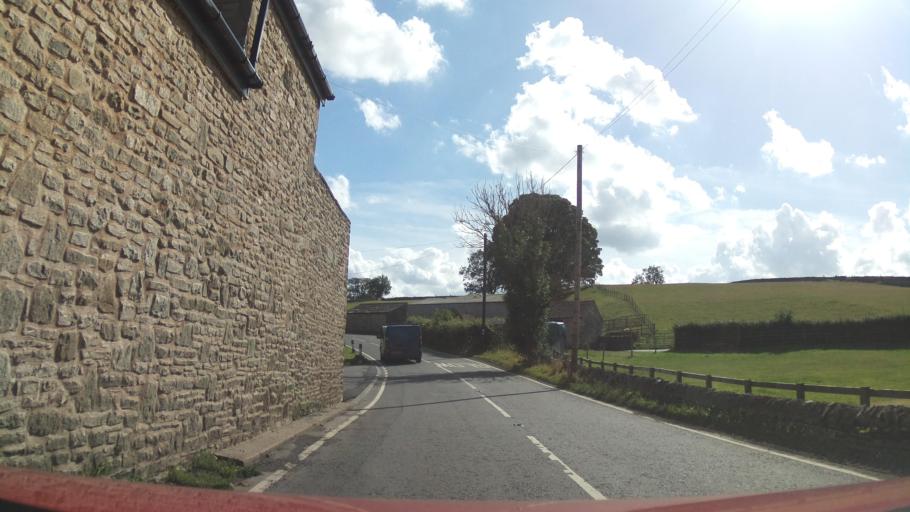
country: GB
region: England
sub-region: North Yorkshire
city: Leyburn
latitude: 54.2937
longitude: -1.8185
